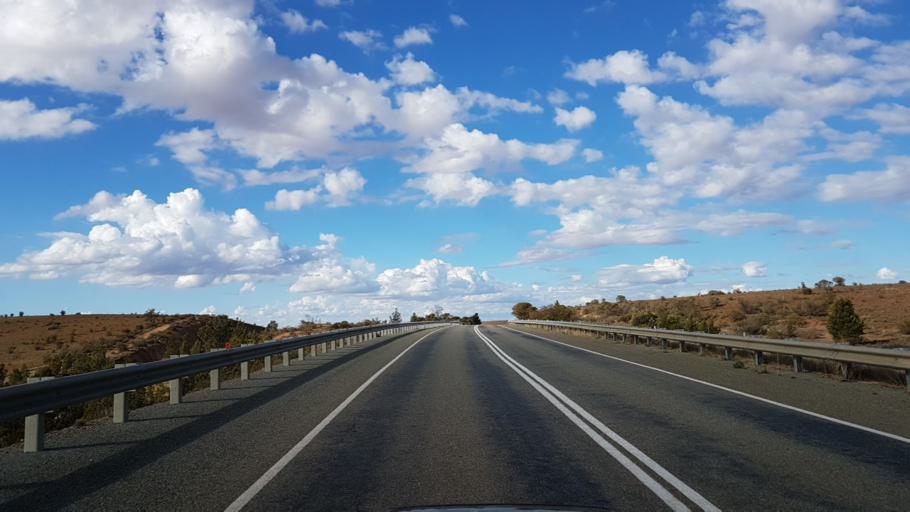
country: AU
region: South Australia
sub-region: Peterborough
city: Peterborough
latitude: -32.9541
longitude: 138.9041
